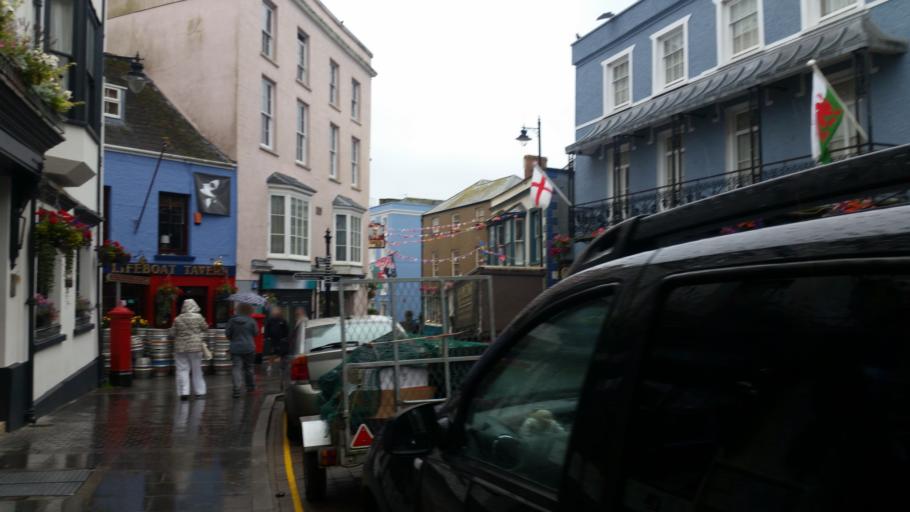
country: GB
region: Wales
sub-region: Pembrokeshire
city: Tenby
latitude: 51.6716
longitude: -4.6984
